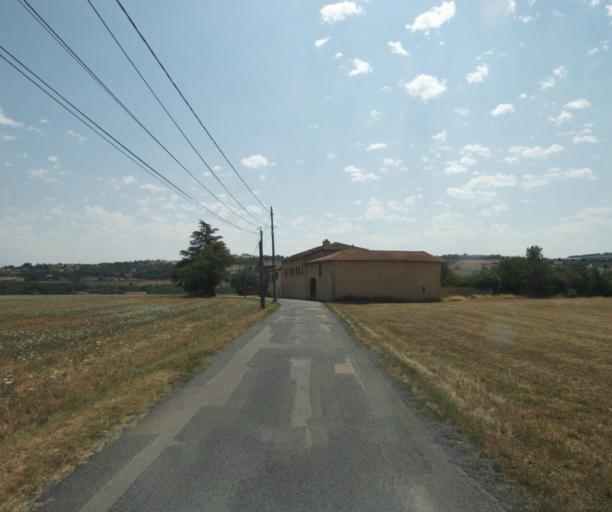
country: FR
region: Rhone-Alpes
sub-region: Departement du Rhone
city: Saint-Germain-Nuelles
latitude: 45.8443
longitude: 4.6266
